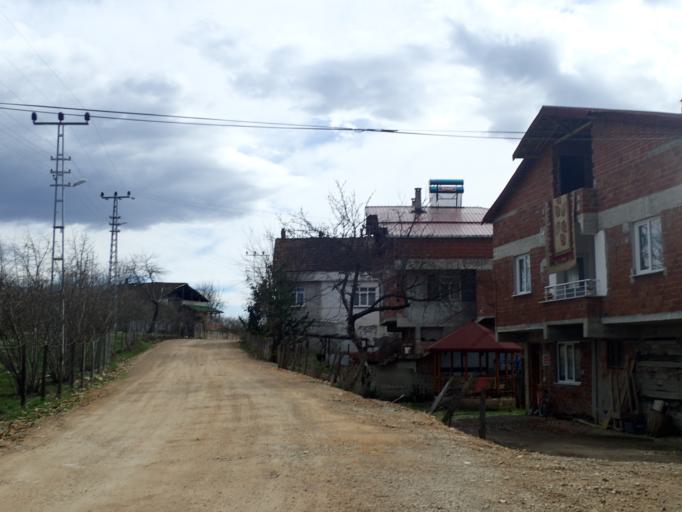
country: TR
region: Ordu
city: Kumru
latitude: 40.9397
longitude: 37.2587
